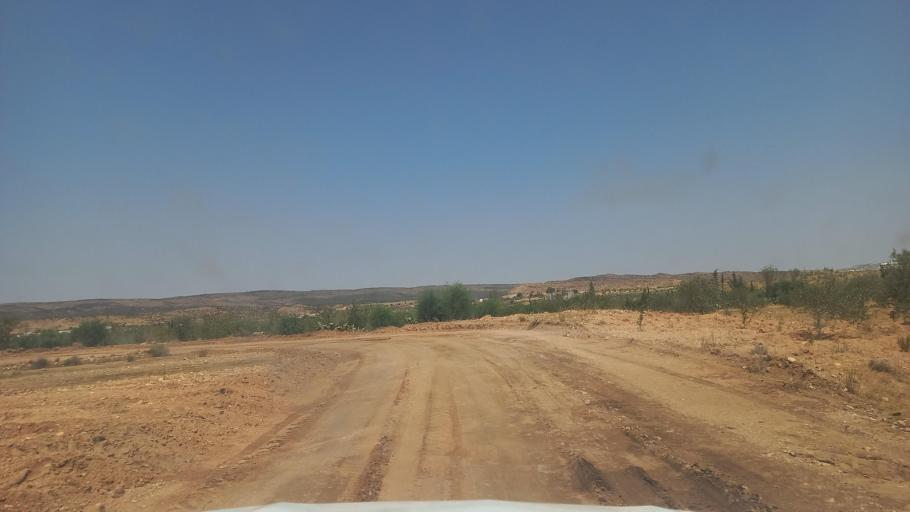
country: TN
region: Al Qasrayn
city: Kasserine
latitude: 35.2928
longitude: 8.9516
